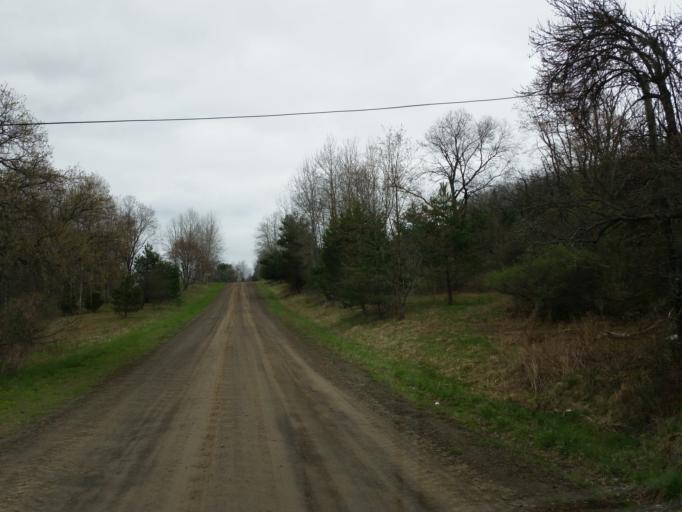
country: US
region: New York
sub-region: Allegany County
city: Andover
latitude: 42.0457
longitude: -77.7528
